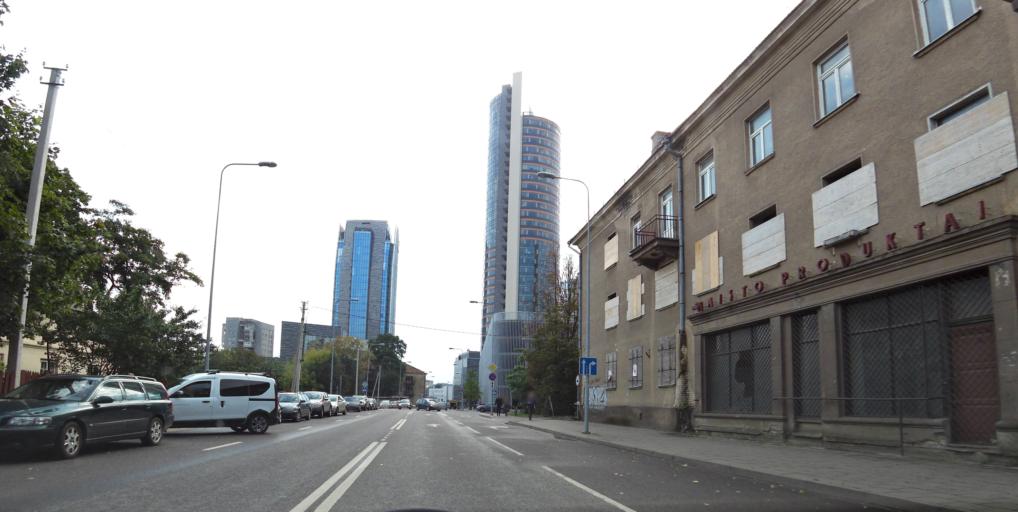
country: LT
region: Vilnius County
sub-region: Vilnius
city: Vilnius
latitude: 54.6976
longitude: 25.2756
